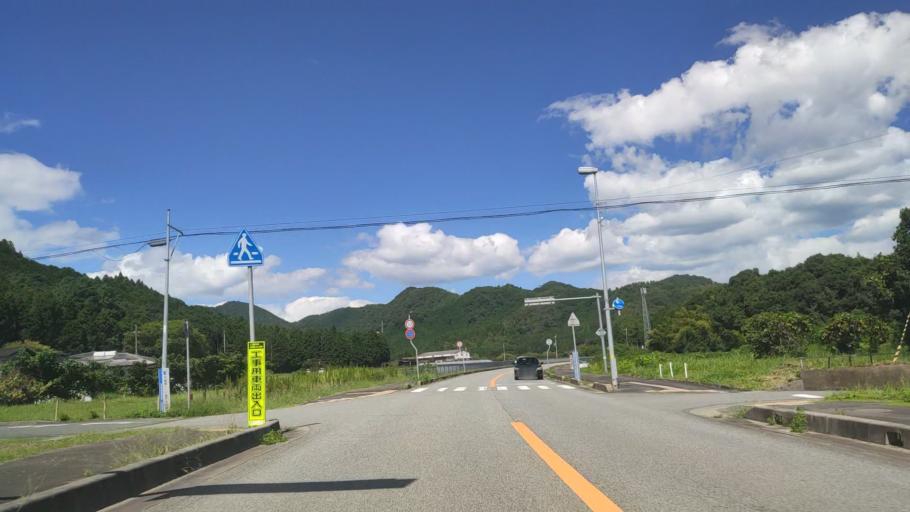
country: JP
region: Kyoto
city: Fukuchiyama
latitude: 35.2401
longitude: 135.1234
